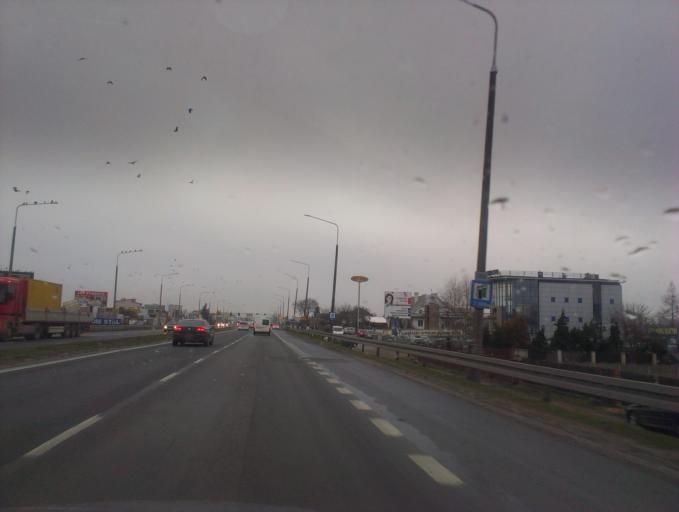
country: PL
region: Masovian Voivodeship
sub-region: Radom
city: Radom
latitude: 51.4323
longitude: 21.1487
